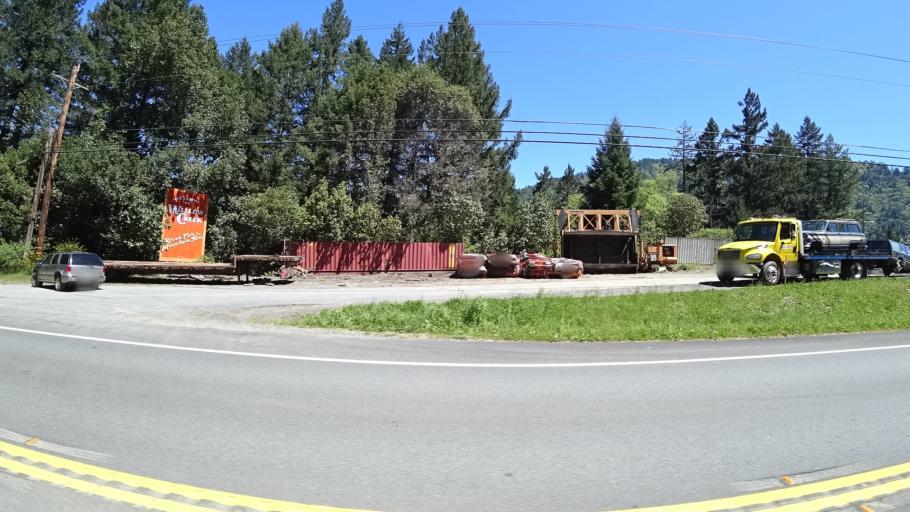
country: US
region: California
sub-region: Humboldt County
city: Willow Creek
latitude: 40.9357
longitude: -123.6252
